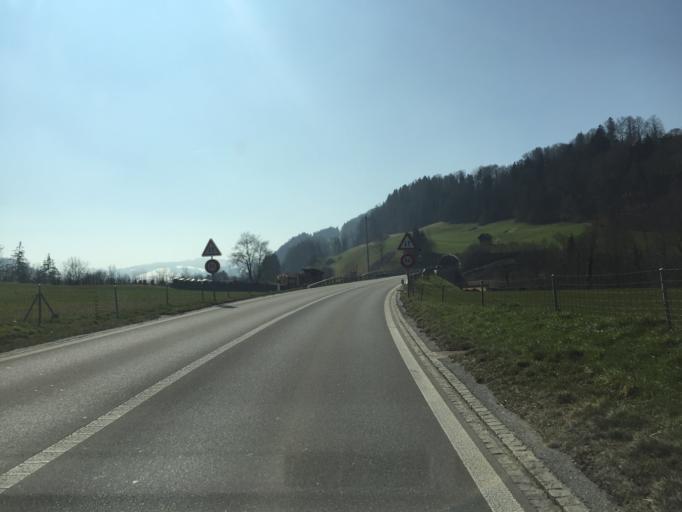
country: CH
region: Saint Gallen
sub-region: Wahlkreis Toggenburg
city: Lichtensteig
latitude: 47.3381
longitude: 9.0817
